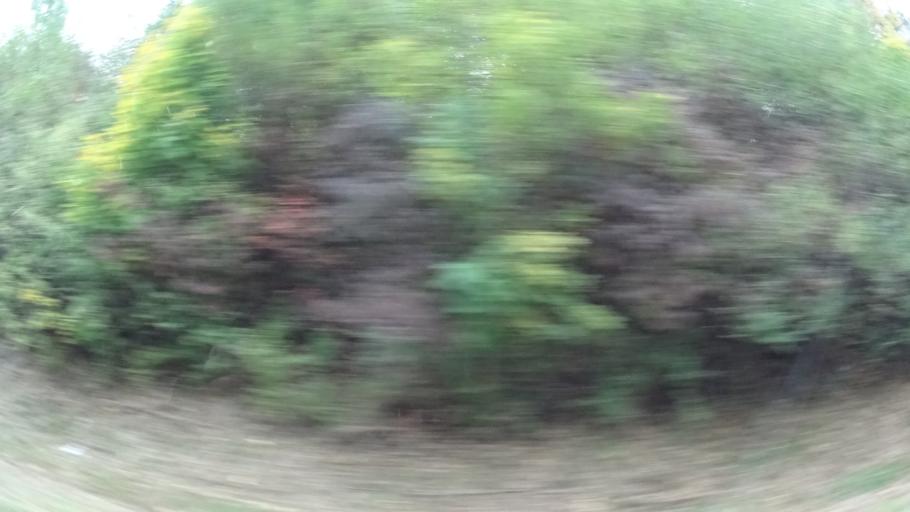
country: DE
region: Hesse
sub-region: Regierungsbezirk Kassel
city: Poppenhausen
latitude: 50.5301
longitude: 9.9333
